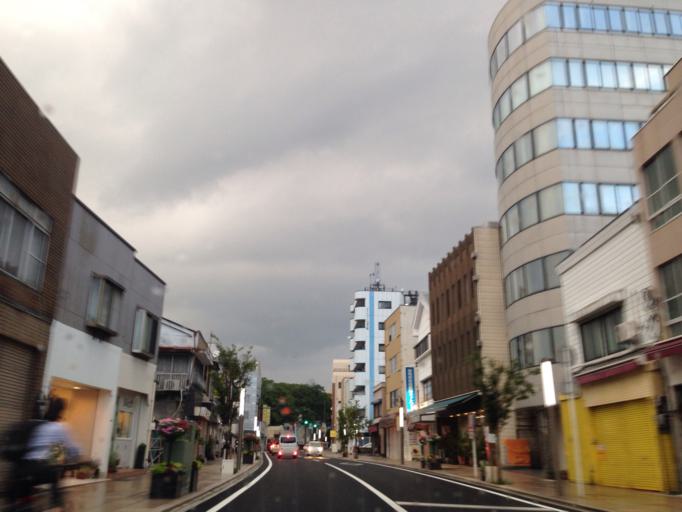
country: JP
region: Shizuoka
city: Mishima
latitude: 35.1213
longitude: 138.9144
